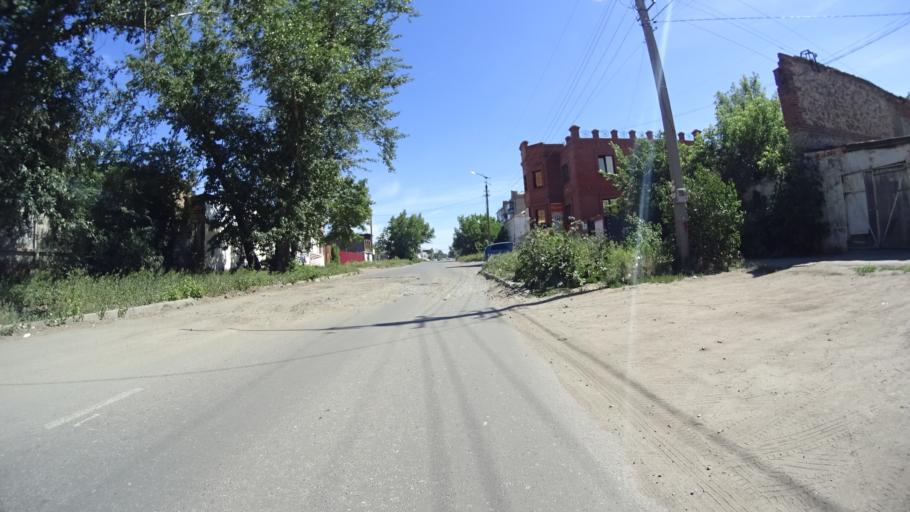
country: RU
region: Chelyabinsk
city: Troitsk
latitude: 54.0886
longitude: 61.5528
